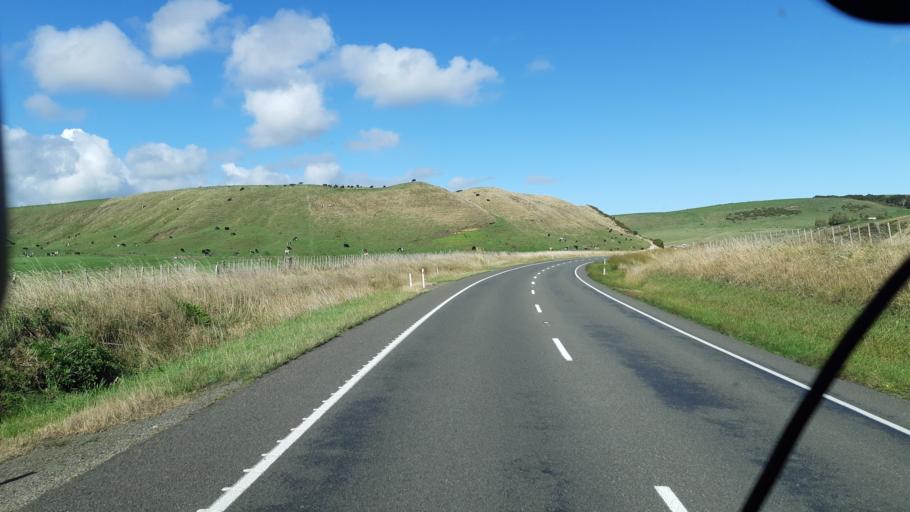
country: NZ
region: Manawatu-Wanganui
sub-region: Wanganui District
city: Wanganui
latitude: -40.0116
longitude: 175.1721
